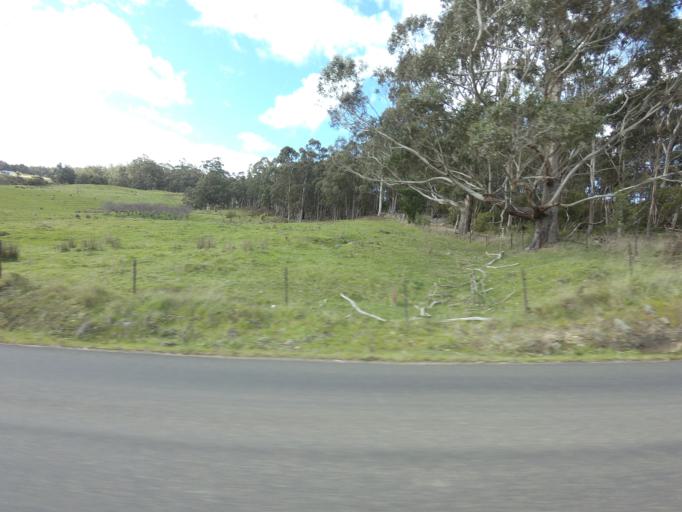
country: AU
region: Tasmania
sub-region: Huon Valley
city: Geeveston
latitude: -43.1883
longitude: 146.9345
